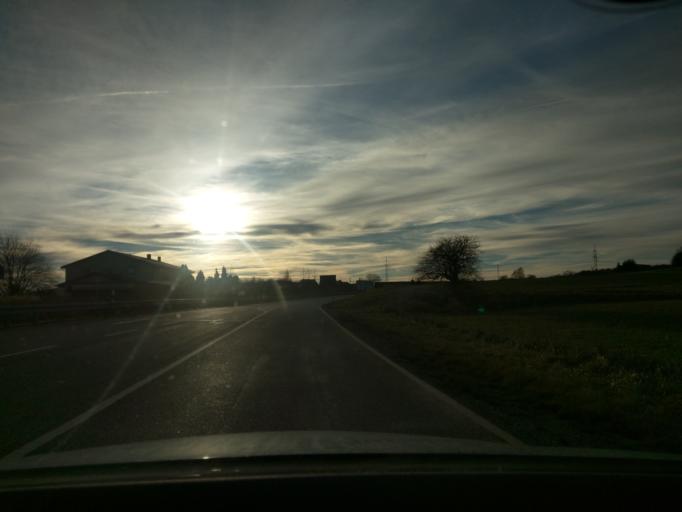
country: DE
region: Bavaria
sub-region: Upper Bavaria
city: Au in der Hallertau
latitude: 48.5664
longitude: 11.7404
